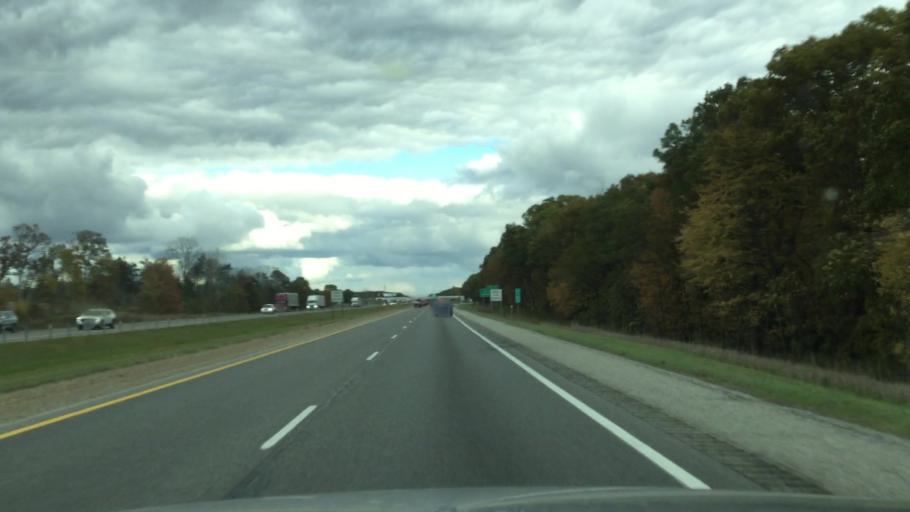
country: US
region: Michigan
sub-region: Kalamazoo County
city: Westwood
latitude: 42.2376
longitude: -85.6904
